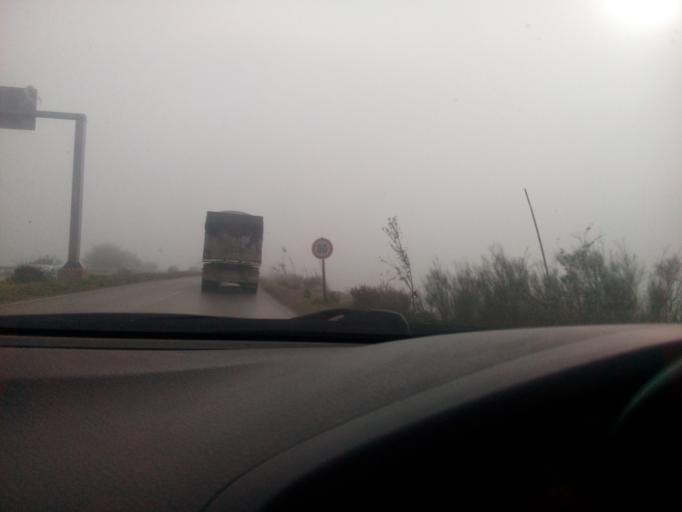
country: DZ
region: Oran
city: Es Senia
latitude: 35.6060
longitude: -0.7401
